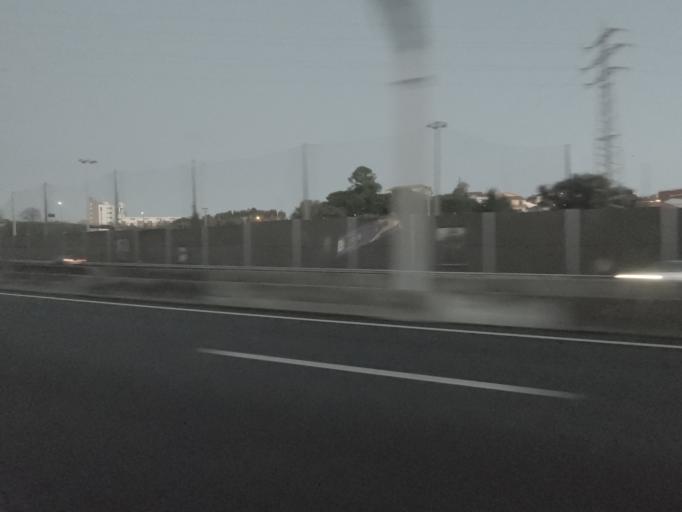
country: PT
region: Porto
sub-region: Maia
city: Pedroucos
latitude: 41.1895
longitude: -8.5943
